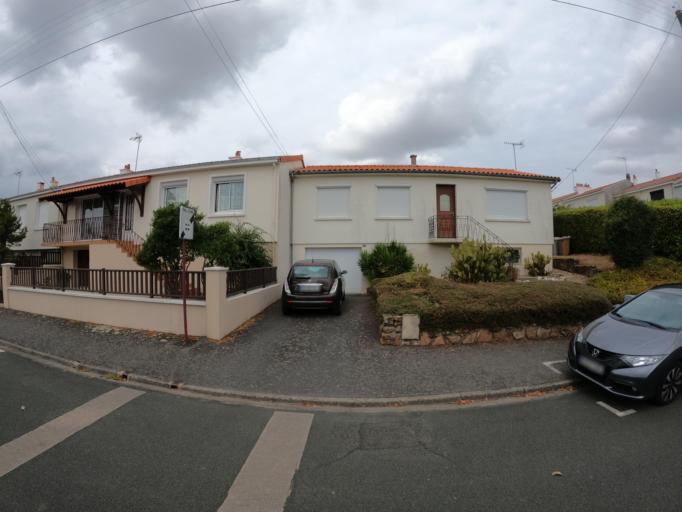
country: FR
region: Pays de la Loire
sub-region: Departement de Maine-et-Loire
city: La Seguiniere
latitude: 47.0648
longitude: -0.9431
